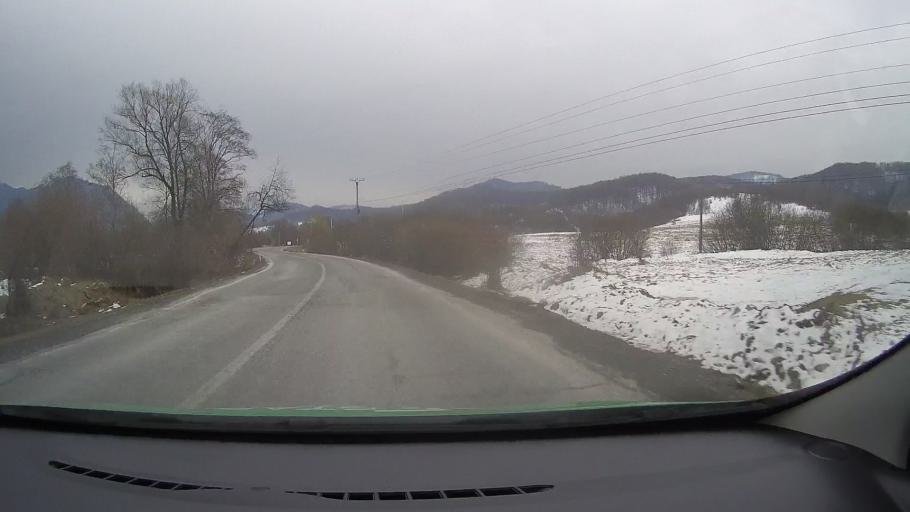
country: RO
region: Brasov
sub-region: Oras Rasnov
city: Rasnov
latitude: 45.5582
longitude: 25.4704
